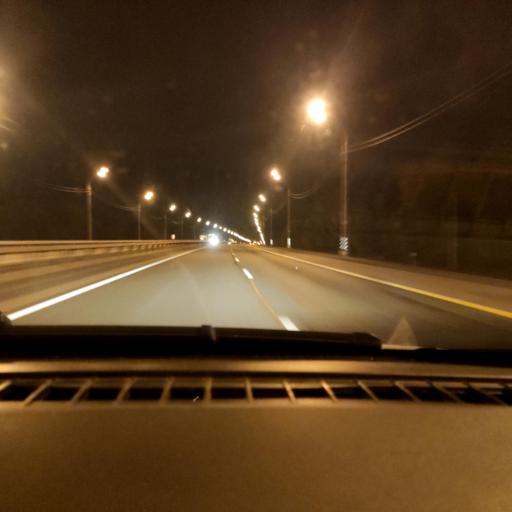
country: RU
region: Lipetsk
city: Khlevnoye
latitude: 52.1747
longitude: 39.1938
